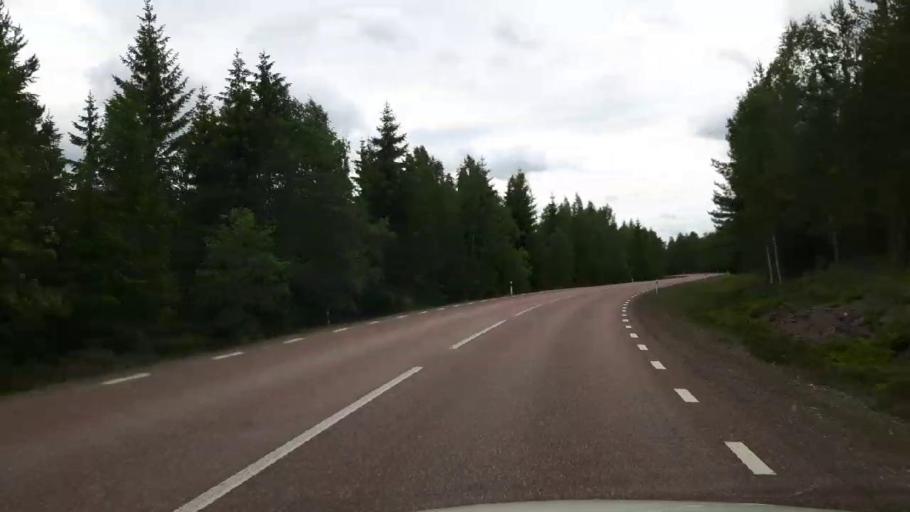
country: SE
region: Dalarna
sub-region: Hedemora Kommun
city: Brunna
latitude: 60.1897
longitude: 16.0003
